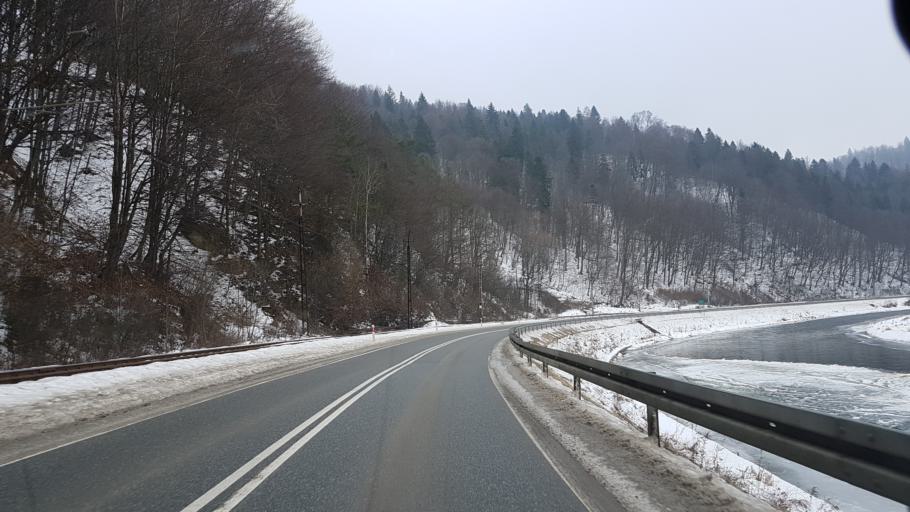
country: PL
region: Lesser Poland Voivodeship
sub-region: Powiat nowosadecki
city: Piwniczna-Zdroj
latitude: 49.4012
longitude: 20.7577
